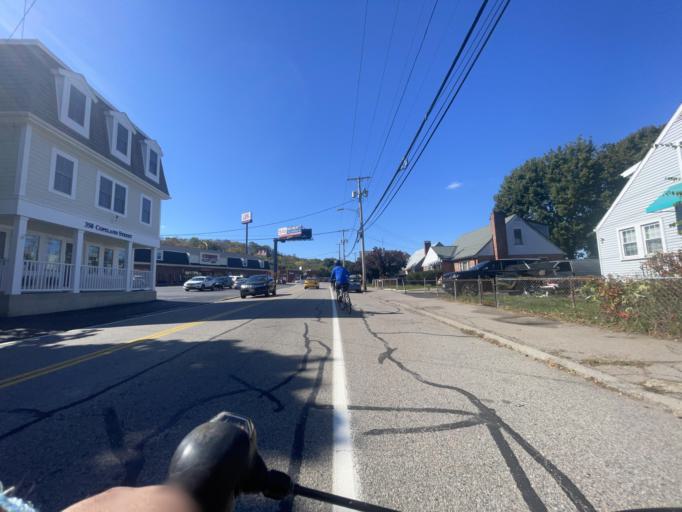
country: US
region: Massachusetts
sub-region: Norfolk County
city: Quincy
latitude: 42.2455
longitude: -71.0304
